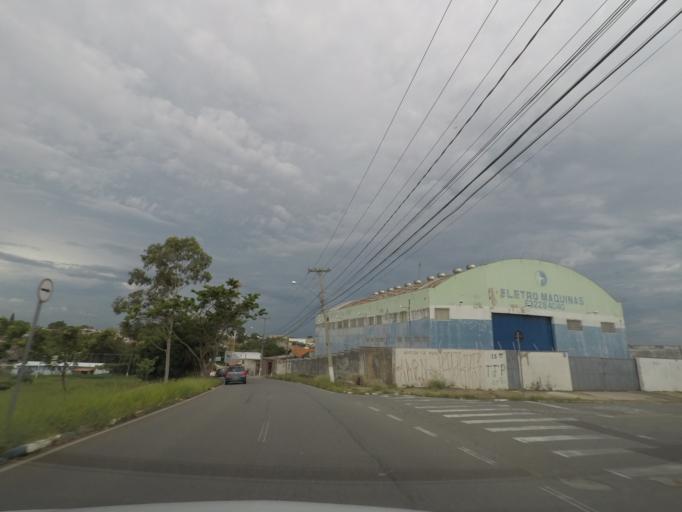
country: BR
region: Sao Paulo
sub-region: Campinas
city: Campinas
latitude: -22.9313
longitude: -47.1082
